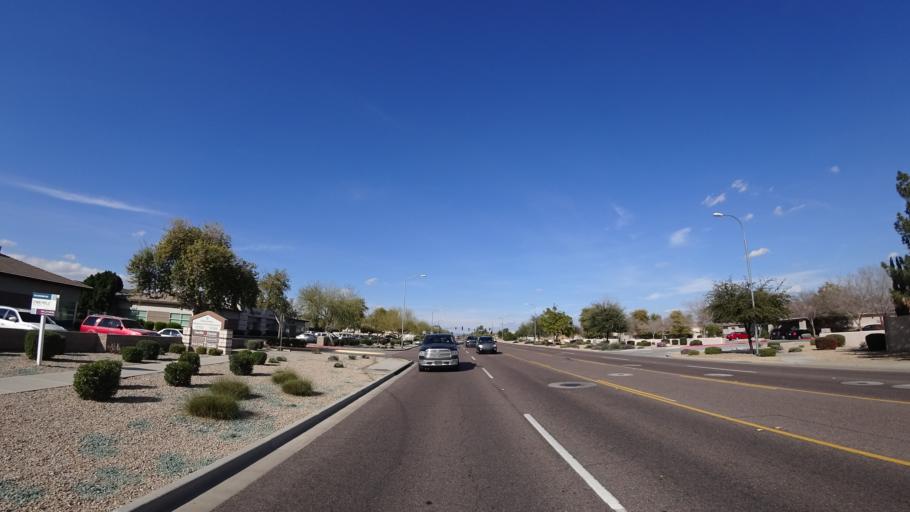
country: US
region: Arizona
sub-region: Maricopa County
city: Peoria
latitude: 33.6230
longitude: -112.2201
